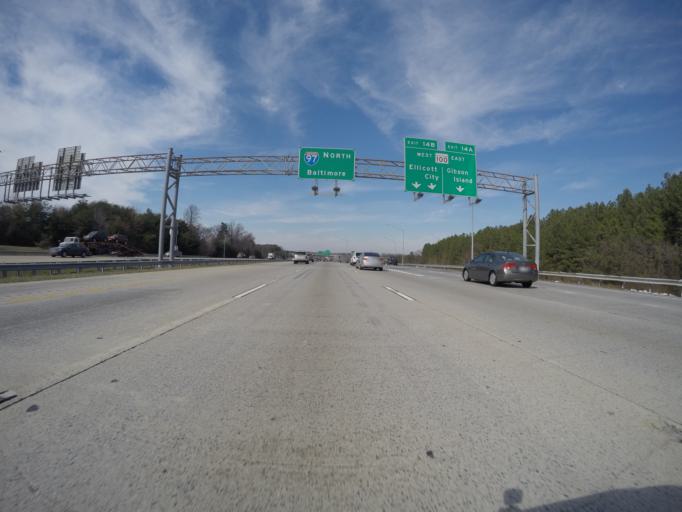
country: US
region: Maryland
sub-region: Anne Arundel County
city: South Gate
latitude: 39.1457
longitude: -76.6446
